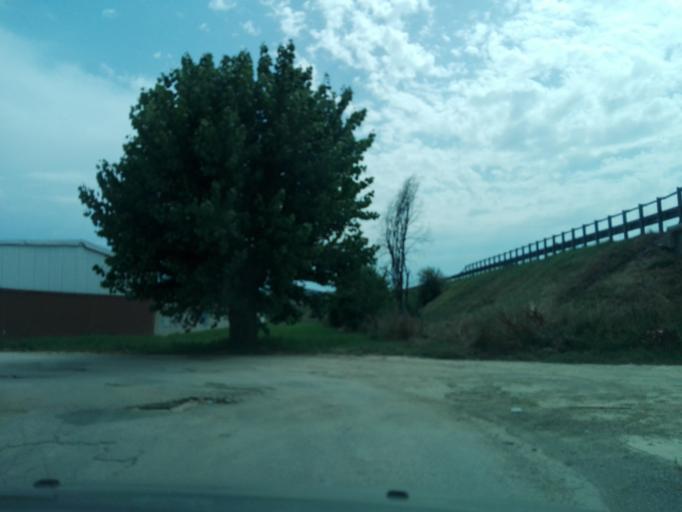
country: IT
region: Abruzzo
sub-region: Provincia di Pescara
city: Cappelle sul Tavo
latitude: 42.4867
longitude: 14.1112
